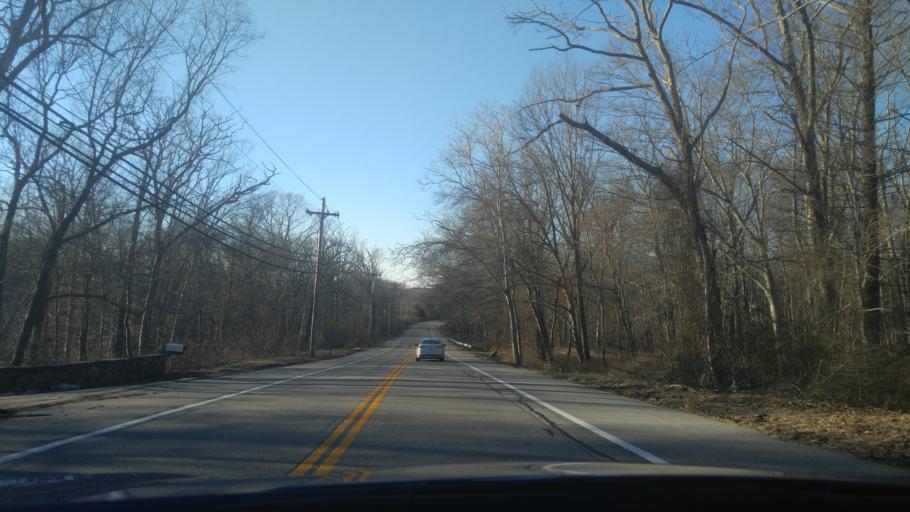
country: US
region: Rhode Island
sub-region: Washington County
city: North Kingstown
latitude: 41.5343
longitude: -71.4335
